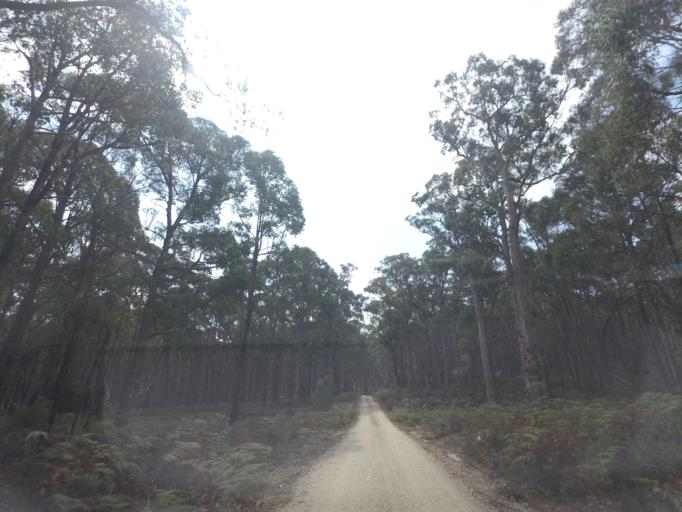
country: AU
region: Victoria
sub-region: Moorabool
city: Bacchus Marsh
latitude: -37.4635
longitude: 144.3739
